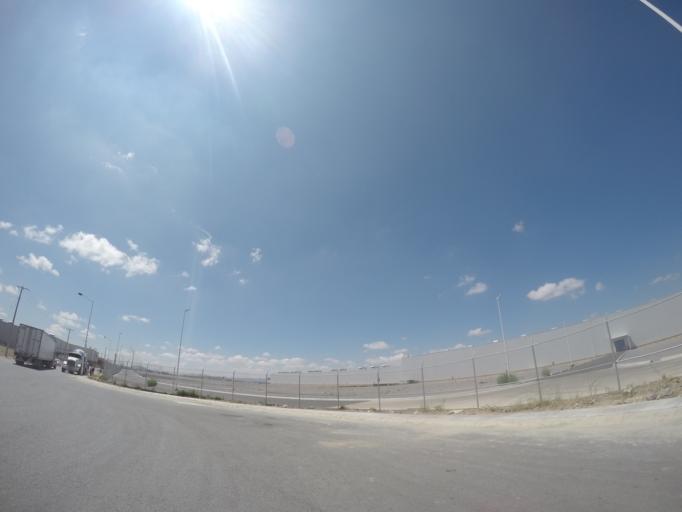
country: MX
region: San Luis Potosi
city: La Pila
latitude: 21.9760
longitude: -100.8799
